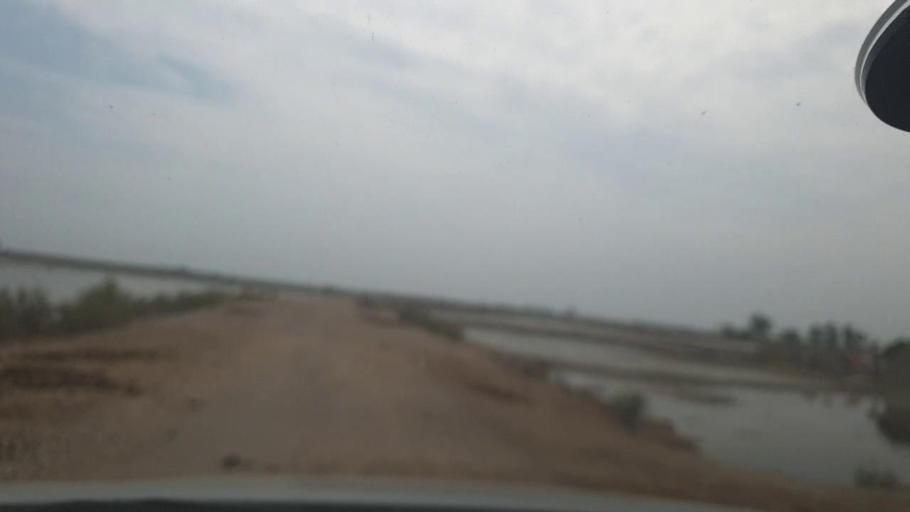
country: PK
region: Balochistan
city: Garhi Khairo
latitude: 28.0161
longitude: 68.0434
